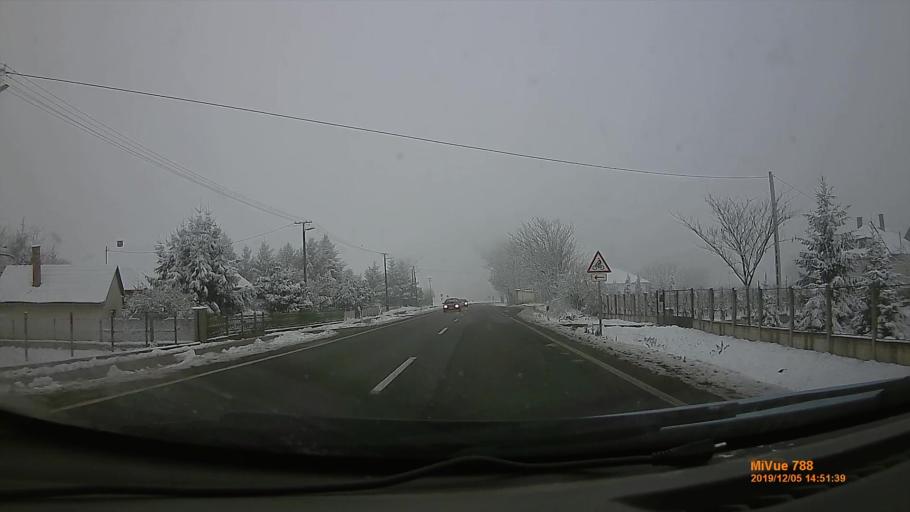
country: HU
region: Szabolcs-Szatmar-Bereg
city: Nyirtelek
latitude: 47.9947
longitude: 21.6545
